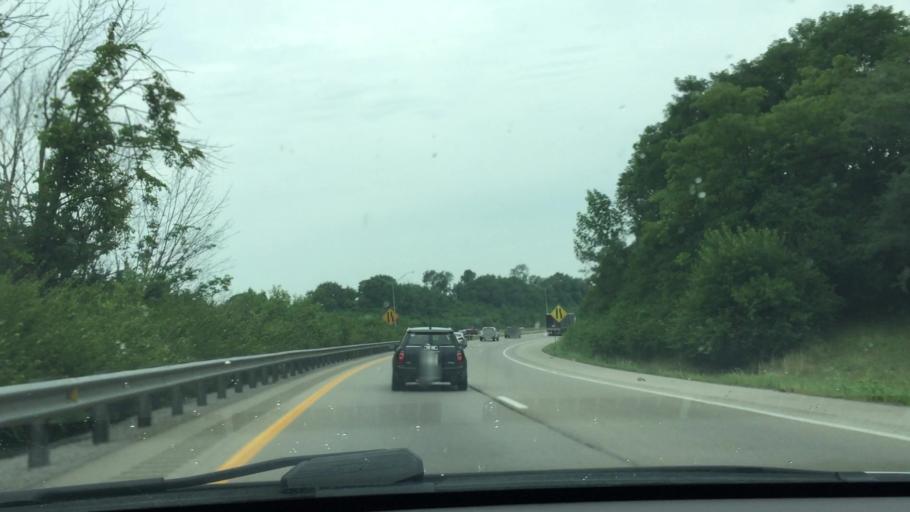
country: US
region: Kentucky
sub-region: Boone County
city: Walton
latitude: 38.8854
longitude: -84.6248
